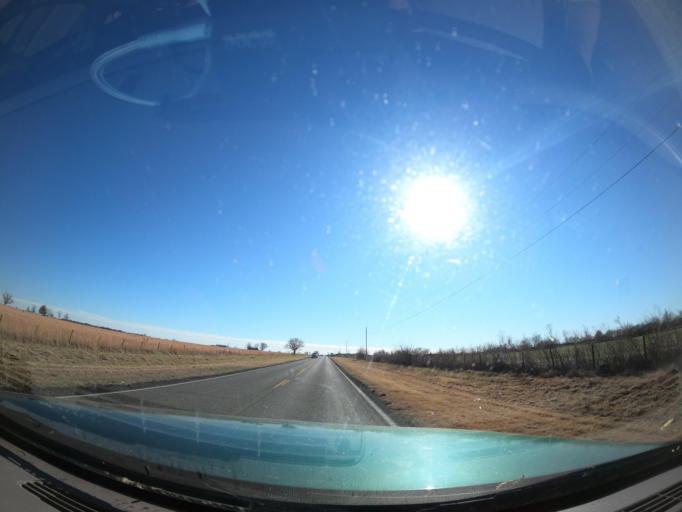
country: US
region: Oklahoma
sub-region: Muskogee County
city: Haskell
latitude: 35.6886
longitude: -95.6422
